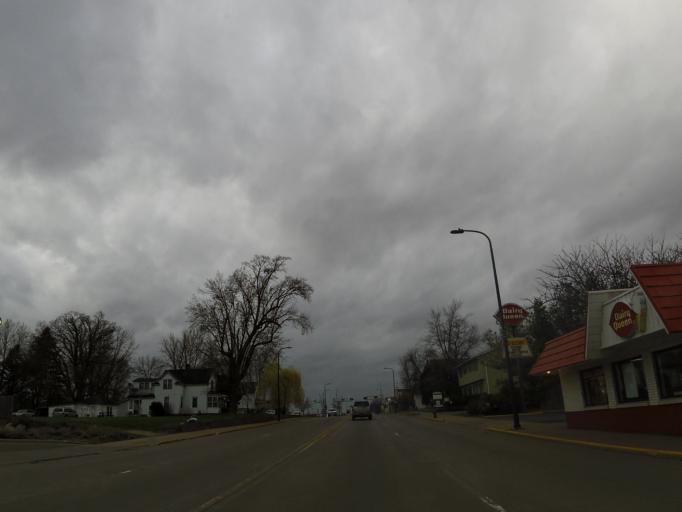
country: US
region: Wisconsin
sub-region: Saint Croix County
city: New Richmond
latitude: 45.1248
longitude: -92.5376
